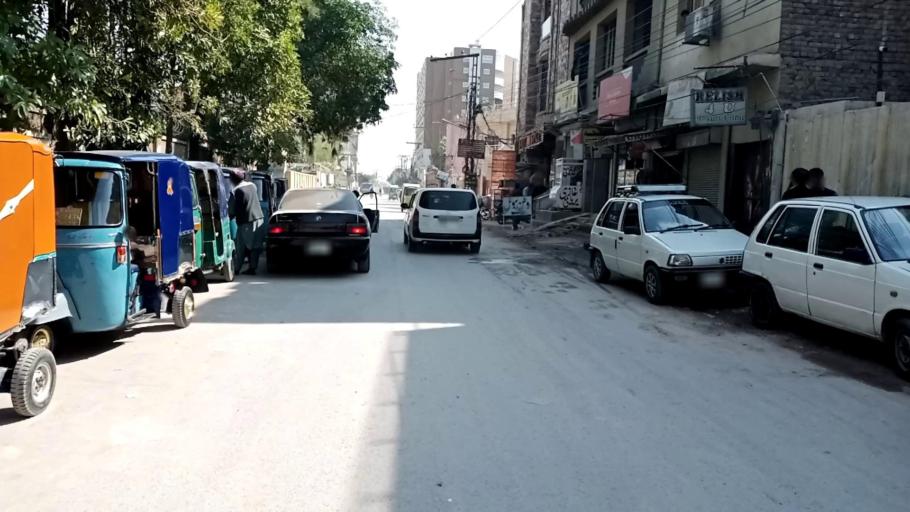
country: PK
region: Khyber Pakhtunkhwa
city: Peshawar
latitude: 33.9952
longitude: 71.5042
